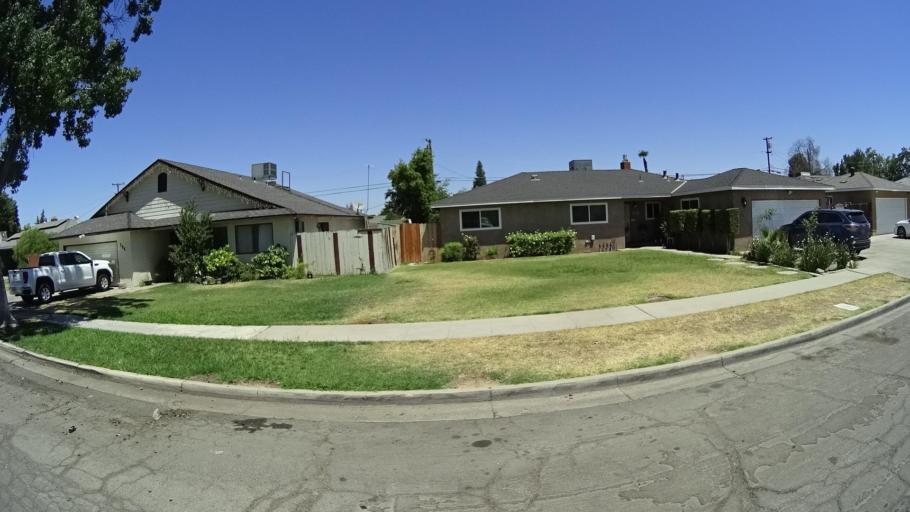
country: US
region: California
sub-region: Fresno County
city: Fresno
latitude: 36.8047
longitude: -119.7598
